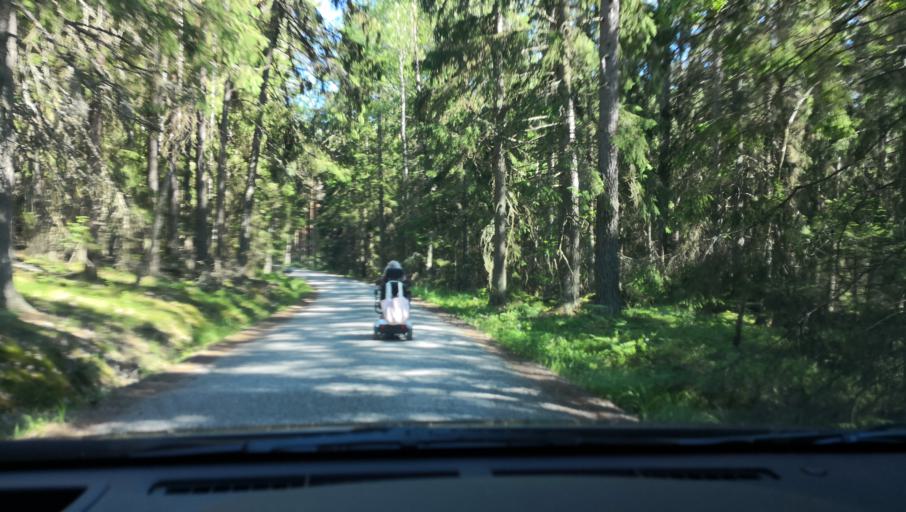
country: SE
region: Soedermanland
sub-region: Eskilstuna Kommun
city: Eskilstuna
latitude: 59.3405
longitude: 16.5647
